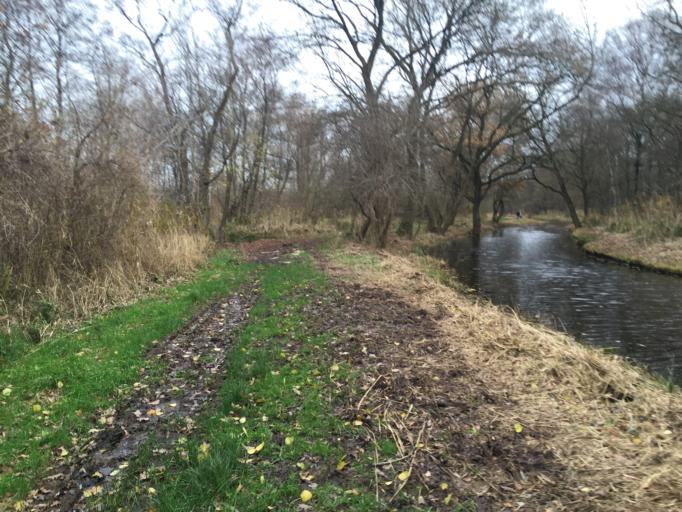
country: NL
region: North Holland
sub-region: Gemeente Weesp
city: Weesp
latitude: 52.2722
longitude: 5.0706
